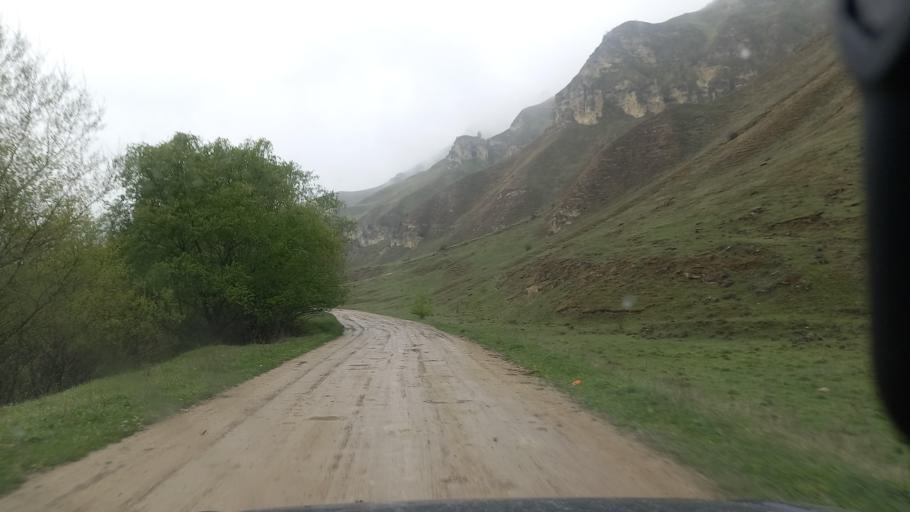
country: RU
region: Kabardino-Balkariya
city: Gundelen
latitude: 43.5984
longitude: 43.0457
